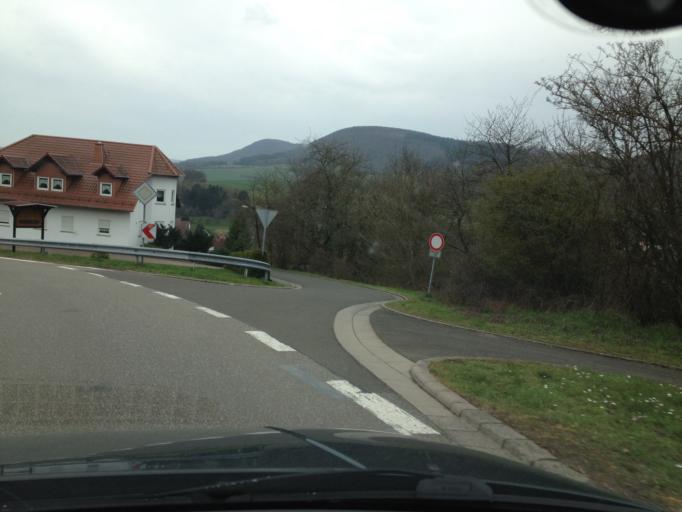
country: DE
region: Rheinland-Pfalz
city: Thallichtenberg
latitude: 49.5588
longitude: 7.3567
